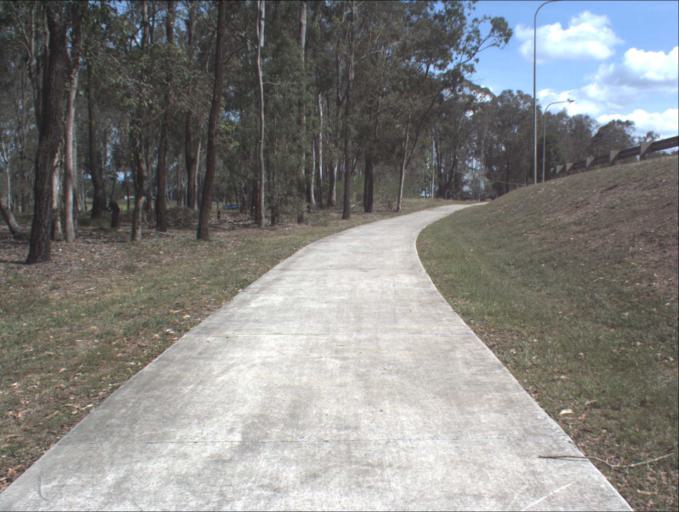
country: AU
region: Queensland
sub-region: Logan
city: Slacks Creek
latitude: -27.6534
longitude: 153.1459
